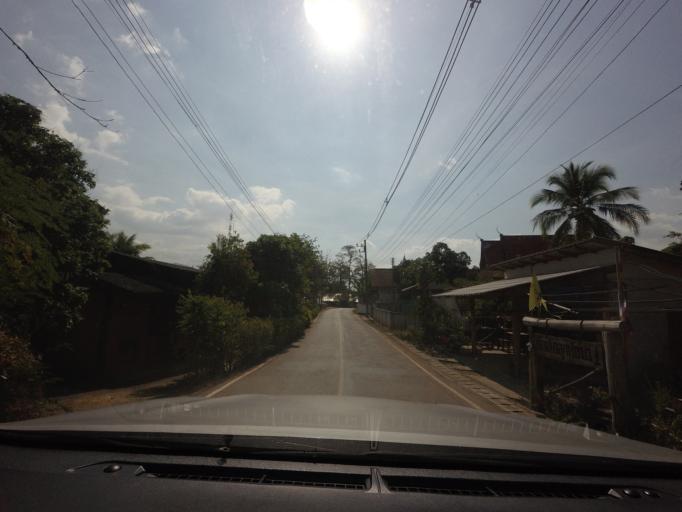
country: TH
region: Mae Hong Son
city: Wiang Nuea
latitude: 19.3963
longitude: 98.4435
